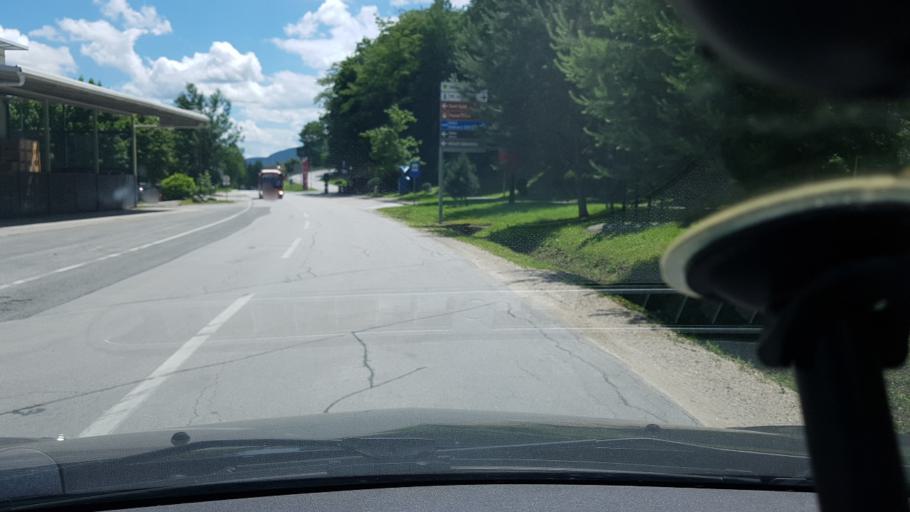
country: SI
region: Zrece
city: Zrece
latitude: 46.3753
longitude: 15.3865
